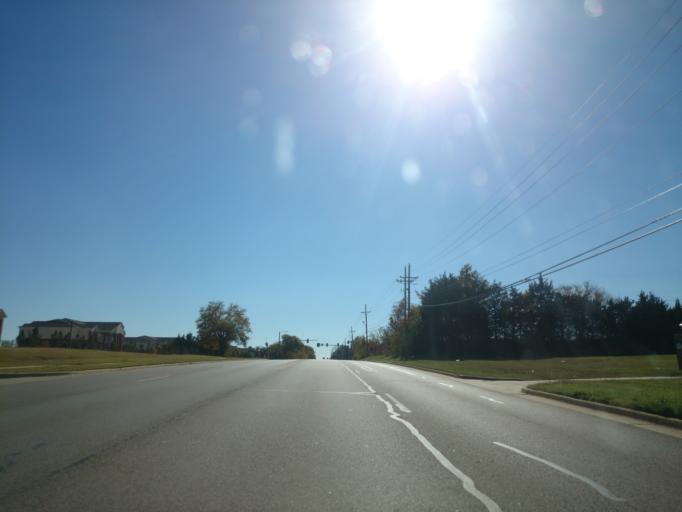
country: US
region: Oklahoma
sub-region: Payne County
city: Stillwater
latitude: 36.1710
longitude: -97.0698
